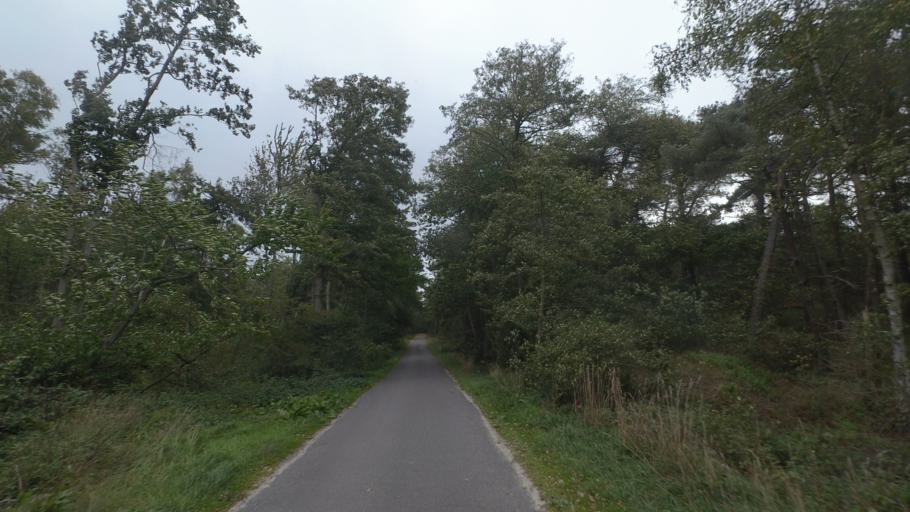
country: DK
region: Capital Region
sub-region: Bornholm Kommune
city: Nexo
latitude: 54.9964
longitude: 15.0383
